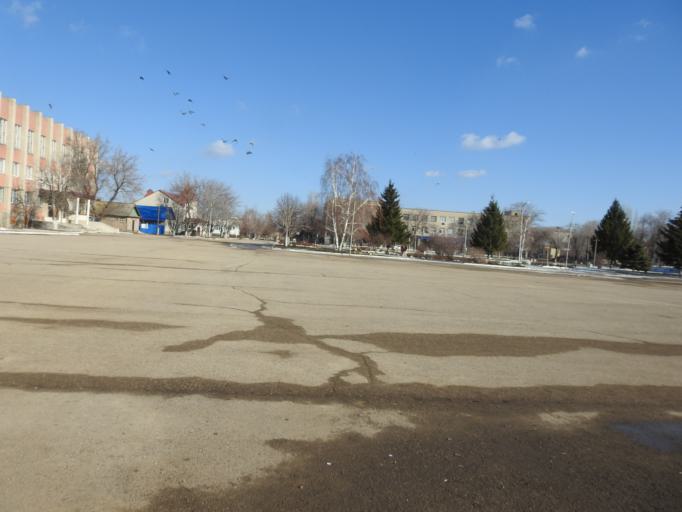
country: RU
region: Saratov
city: Yershov
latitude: 51.3502
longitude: 48.2652
